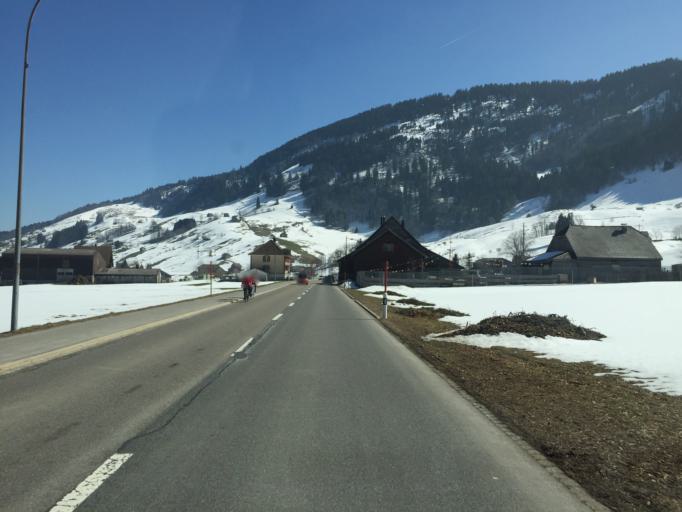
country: CH
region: Saint Gallen
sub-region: Wahlkreis Sarganserland
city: Quarten
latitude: 47.1851
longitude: 9.2527
